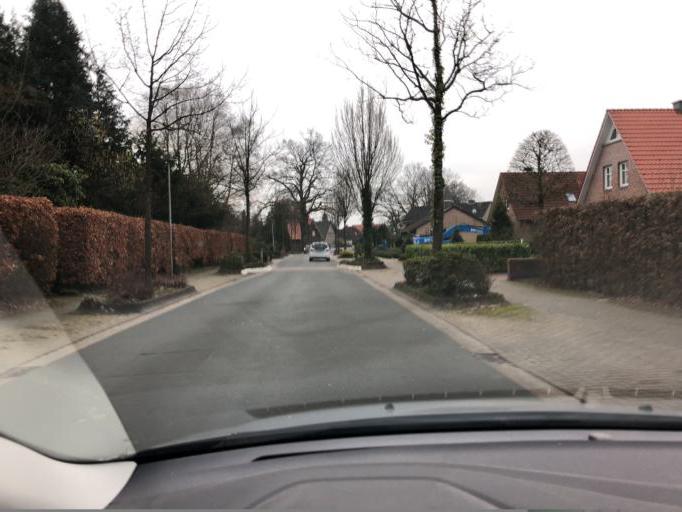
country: DE
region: Lower Saxony
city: Bad Zwischenahn
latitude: 53.1747
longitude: 8.0101
